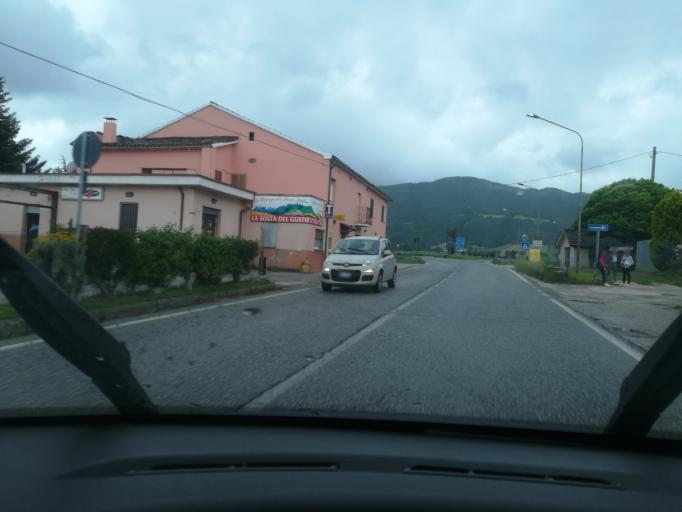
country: IT
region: The Marches
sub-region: Provincia di Macerata
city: Cessapalombo
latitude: 43.0769
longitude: 13.2808
